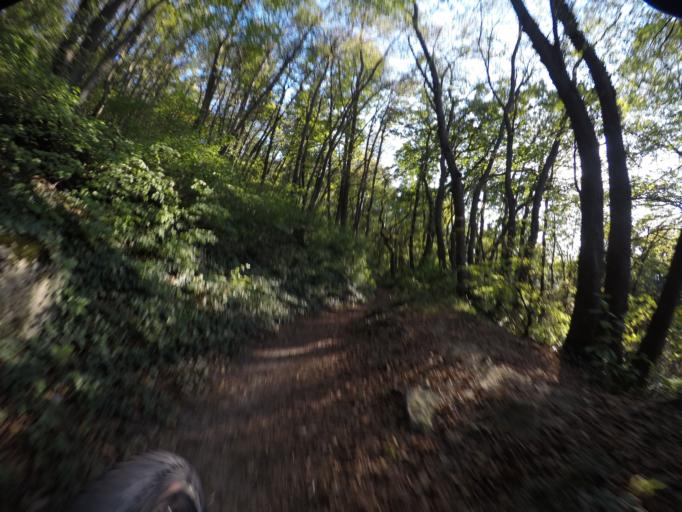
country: AT
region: Lower Austria
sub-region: Politischer Bezirk Bruck an der Leitha
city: Mannersdorf am Leithagebirge
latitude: 47.9677
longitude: 16.6021
